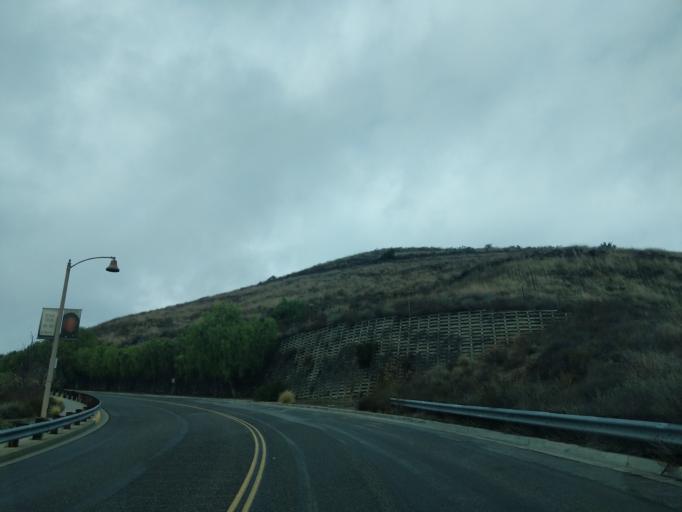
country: US
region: California
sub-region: Ventura County
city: Simi Valley
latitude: 34.2575
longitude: -118.8112
